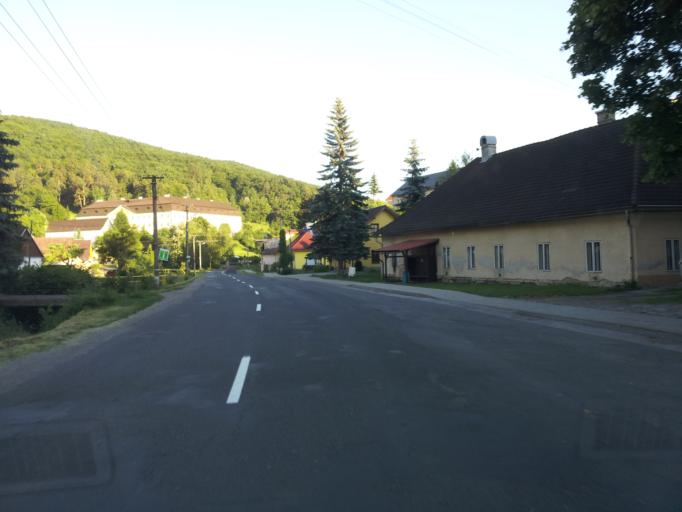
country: SK
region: Banskobystricky
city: Svaety Anton
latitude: 48.4243
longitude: 18.9398
